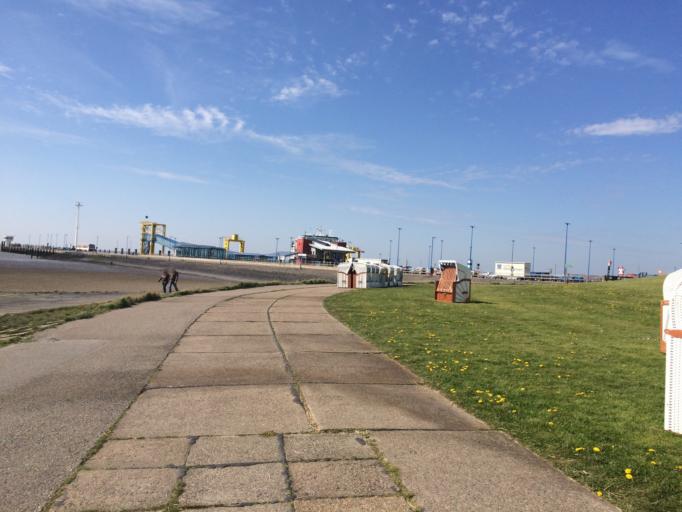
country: DE
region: Schleswig-Holstein
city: Dagebull
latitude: 54.7288
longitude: 8.6929
